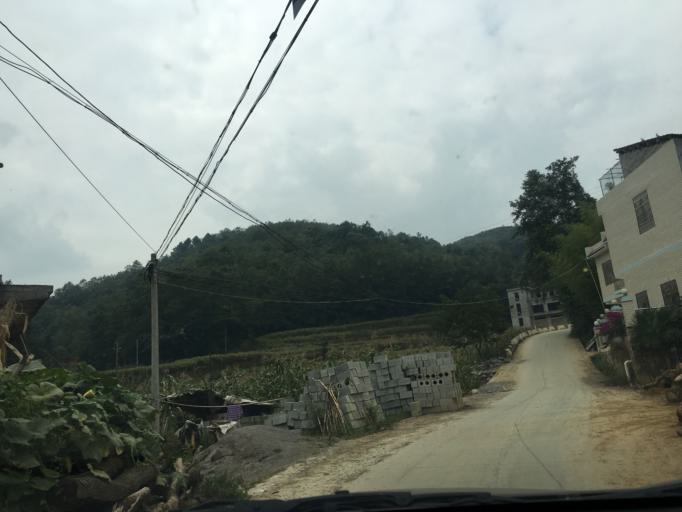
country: CN
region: Guangxi Zhuangzu Zizhiqu
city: Xinzhou
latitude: 25.5434
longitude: 105.5787
